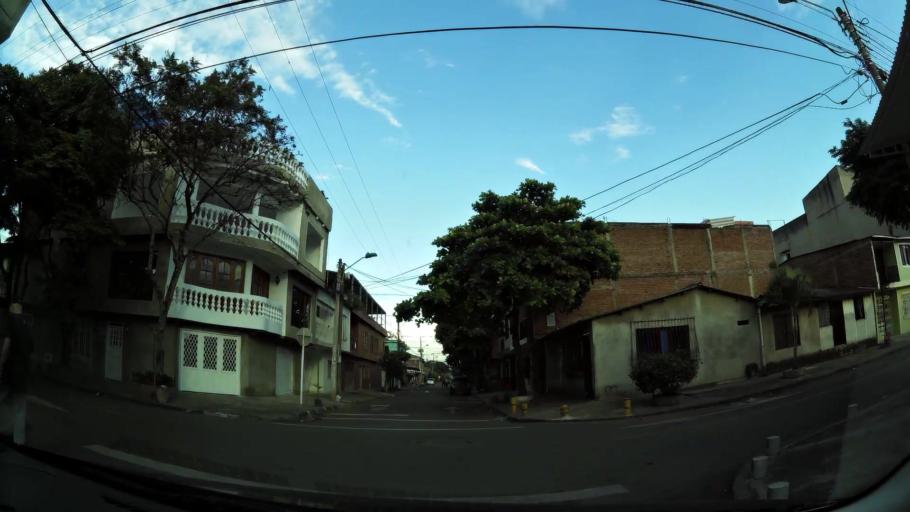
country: CO
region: Valle del Cauca
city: Cali
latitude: 3.4262
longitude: -76.5099
